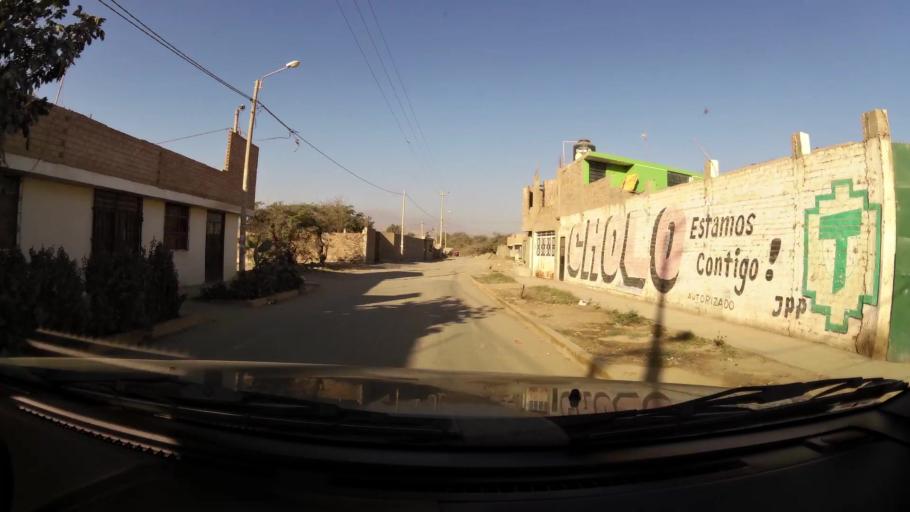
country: PE
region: Ica
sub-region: Provincia de Ica
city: Ica
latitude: -14.0664
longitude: -75.7182
